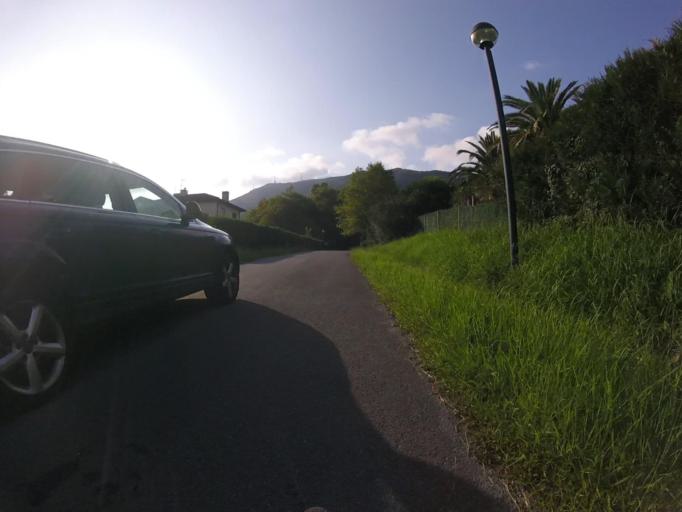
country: ES
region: Basque Country
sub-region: Provincia de Guipuzcoa
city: Irun
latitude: 43.3403
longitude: -1.8365
